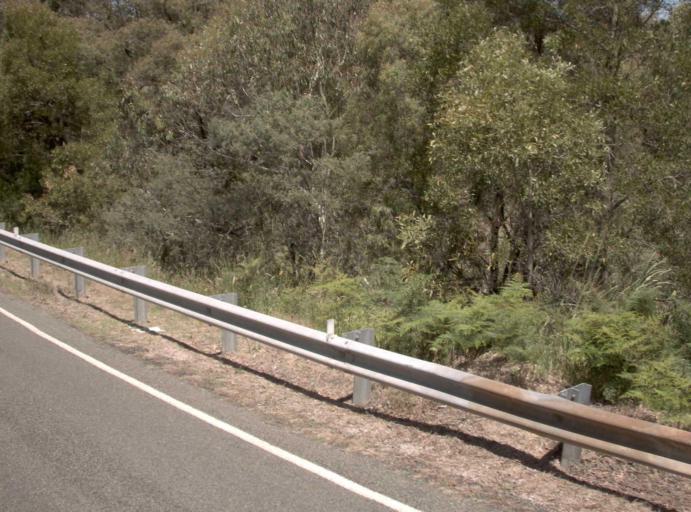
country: AU
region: Victoria
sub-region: Alpine
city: Mount Beauty
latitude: -37.1547
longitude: 147.6523
